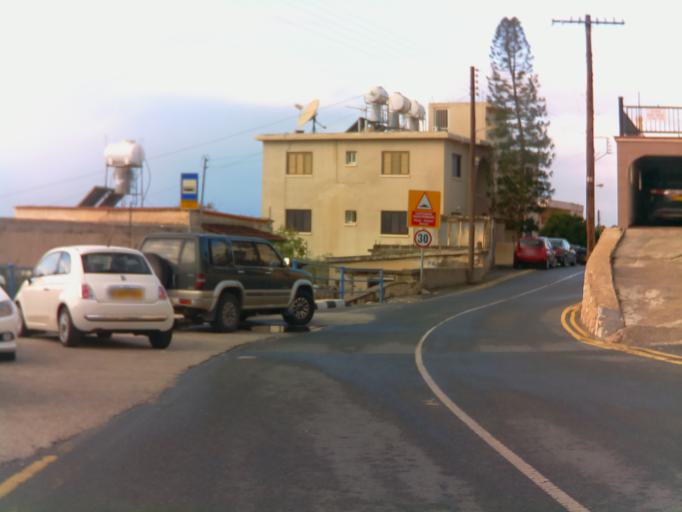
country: CY
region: Pafos
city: Pegeia
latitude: 34.8846
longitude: 32.3814
